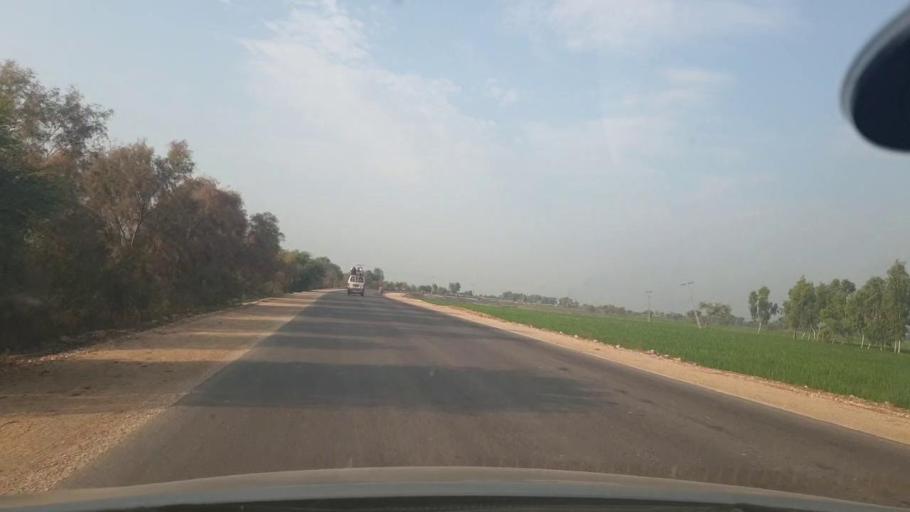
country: PK
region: Sindh
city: Jacobabad
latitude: 28.2400
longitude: 68.3921
